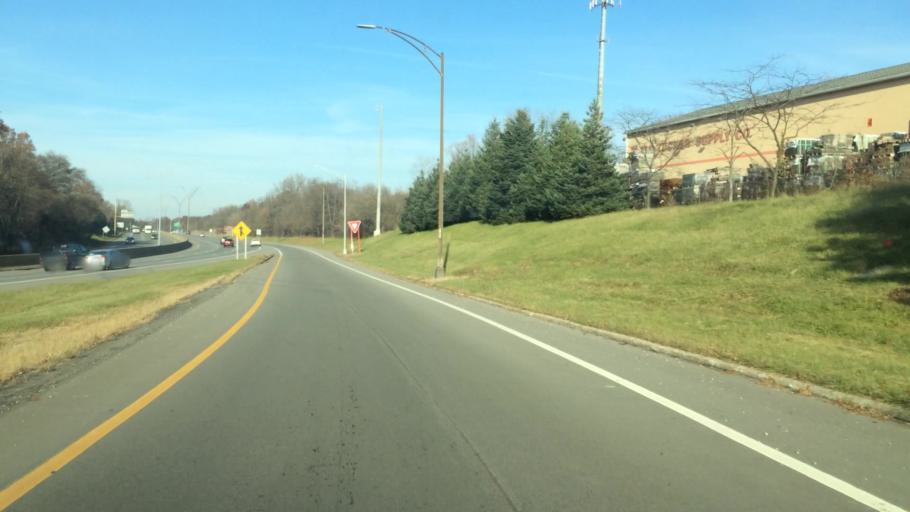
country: US
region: Ohio
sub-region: Summit County
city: Cuyahoga Falls
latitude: 41.1489
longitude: -81.4724
